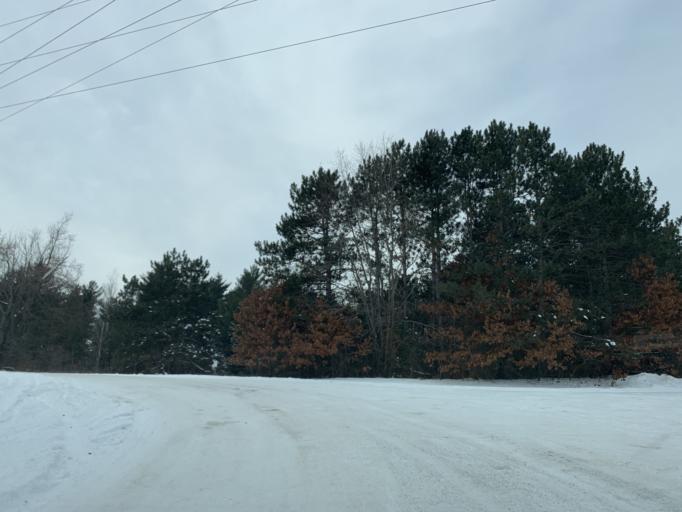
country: US
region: Minnesota
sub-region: Washington County
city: Forest Lake
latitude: 45.2901
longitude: -93.0088
